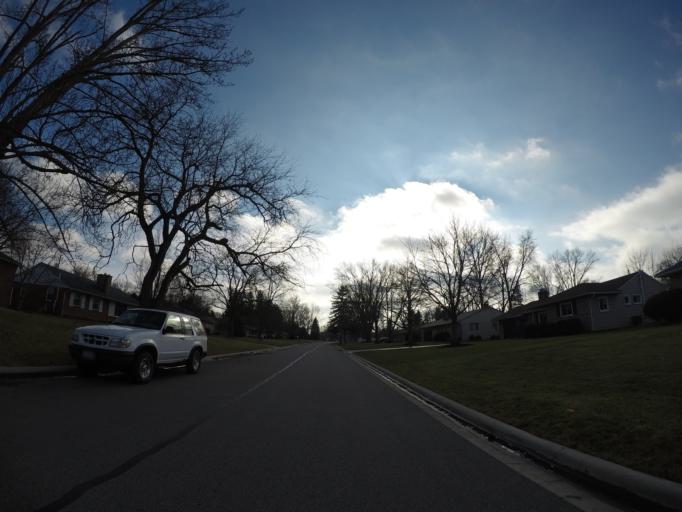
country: US
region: Ohio
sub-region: Franklin County
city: Upper Arlington
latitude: 40.0263
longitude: -83.0651
